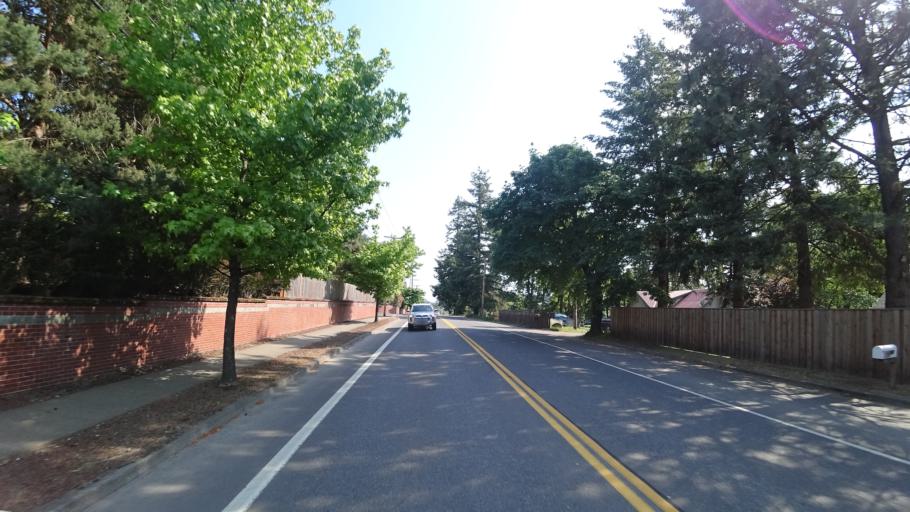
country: US
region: Oregon
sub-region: Clackamas County
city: Sunnyside
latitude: 45.4316
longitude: -122.5381
